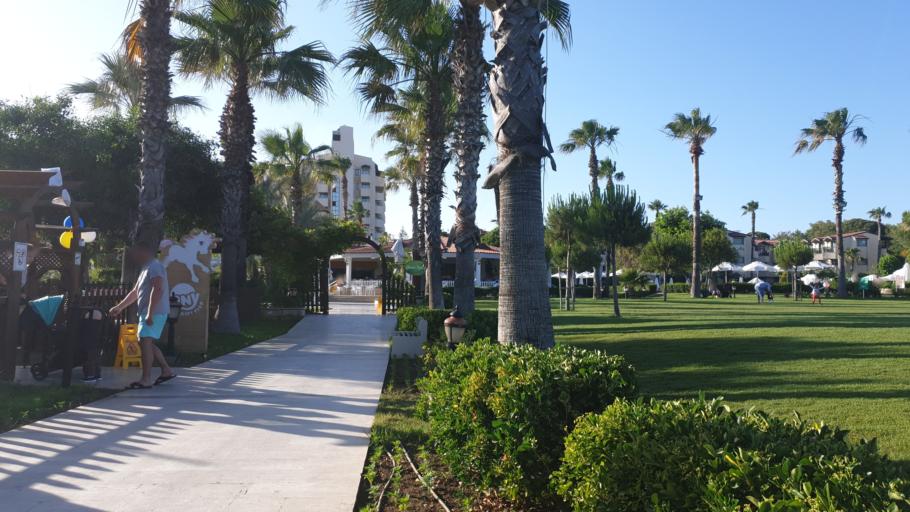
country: TR
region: Antalya
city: Belek
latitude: 36.8563
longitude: 31.0234
